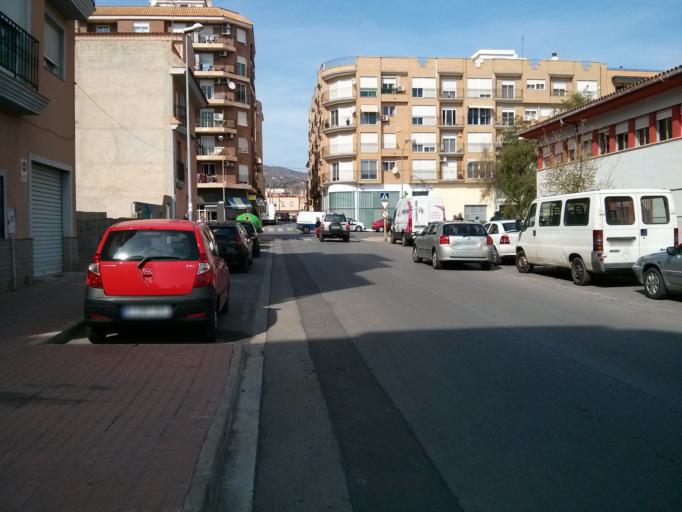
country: ES
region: Valencia
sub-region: Provincia de Castello
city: Alfondeguilla
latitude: 39.8217
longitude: -0.2250
